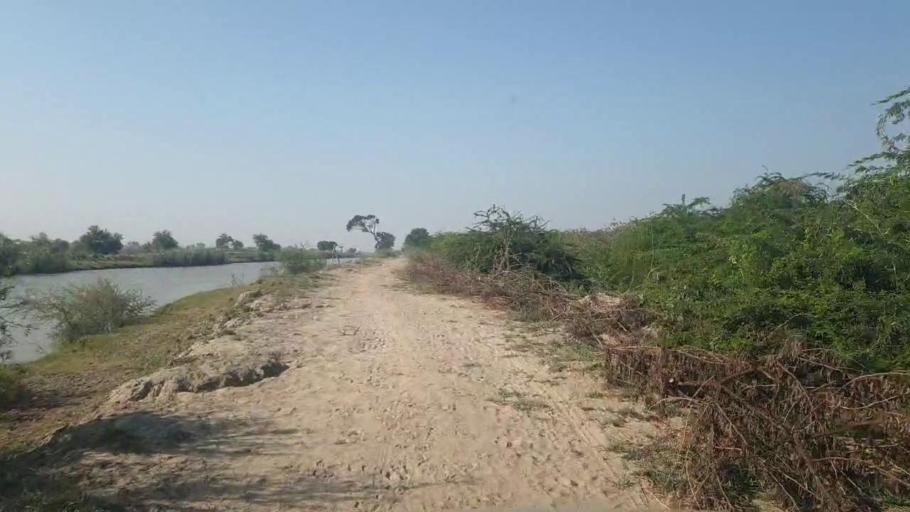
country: PK
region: Sindh
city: Badin
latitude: 24.6996
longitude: 68.8783
